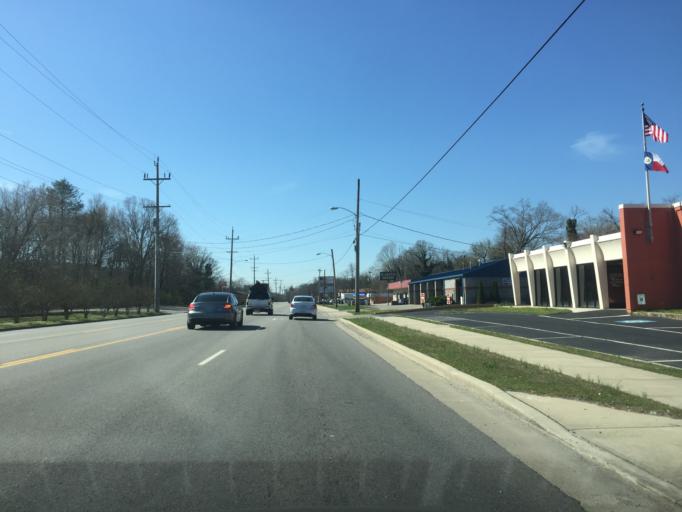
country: US
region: Tennessee
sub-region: Hamilton County
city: Red Bank
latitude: 35.1060
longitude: -85.2978
